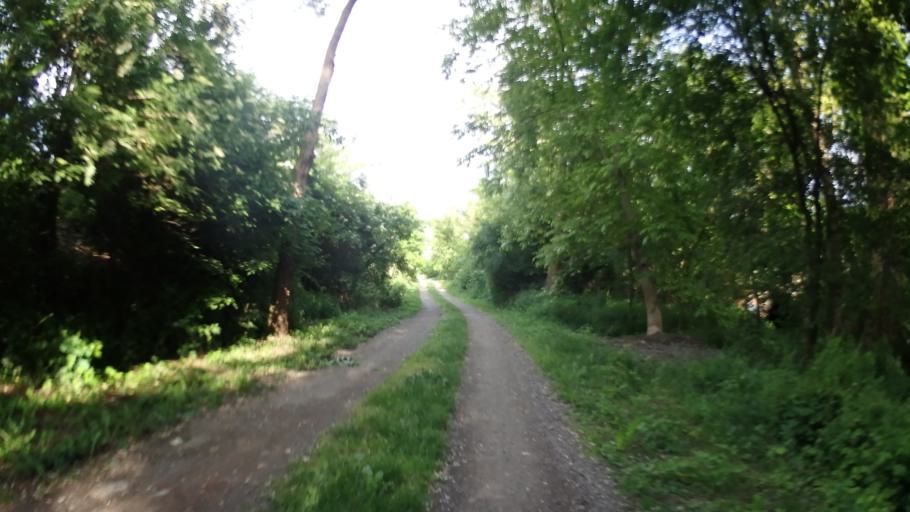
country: CZ
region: South Moravian
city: Moravany
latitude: 49.1599
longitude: 16.6035
